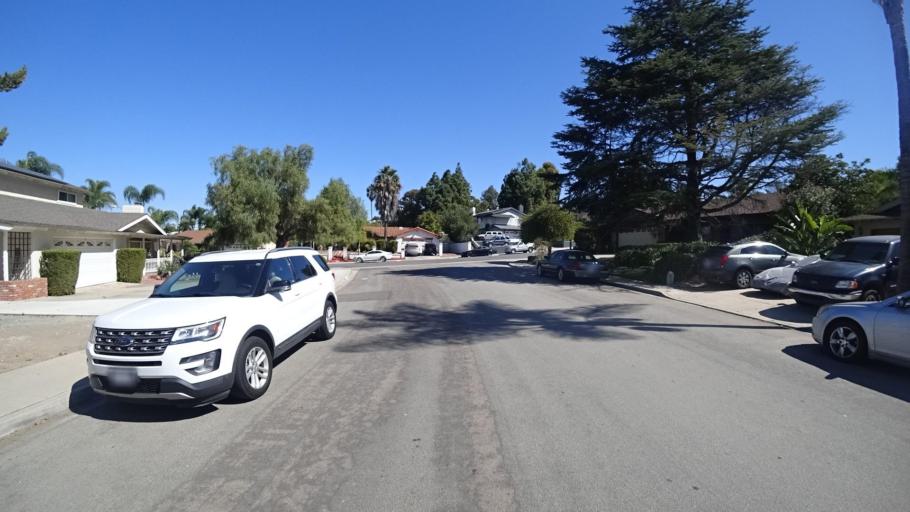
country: US
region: California
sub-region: San Diego County
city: Bonita
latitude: 32.6654
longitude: -117.0215
